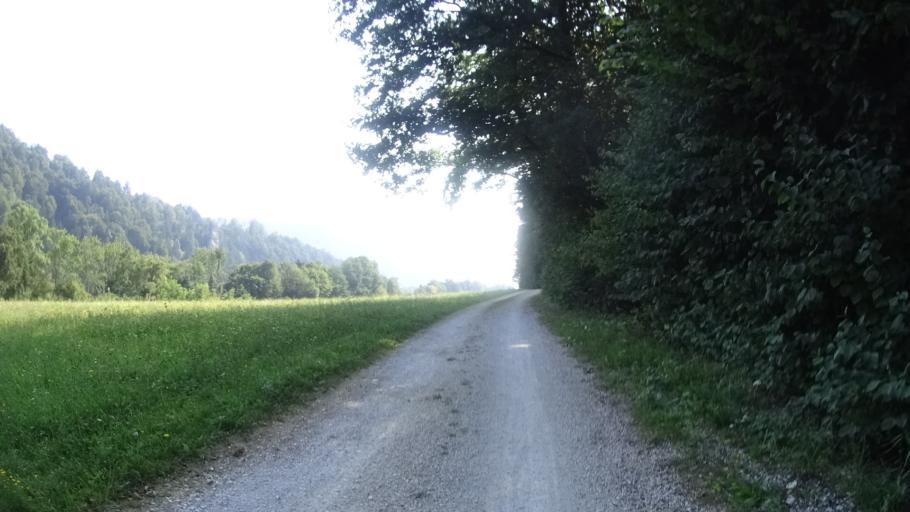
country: AT
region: Carinthia
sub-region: Politischer Bezirk Klagenfurt Land
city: Ferlach
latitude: 46.5449
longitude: 14.3223
